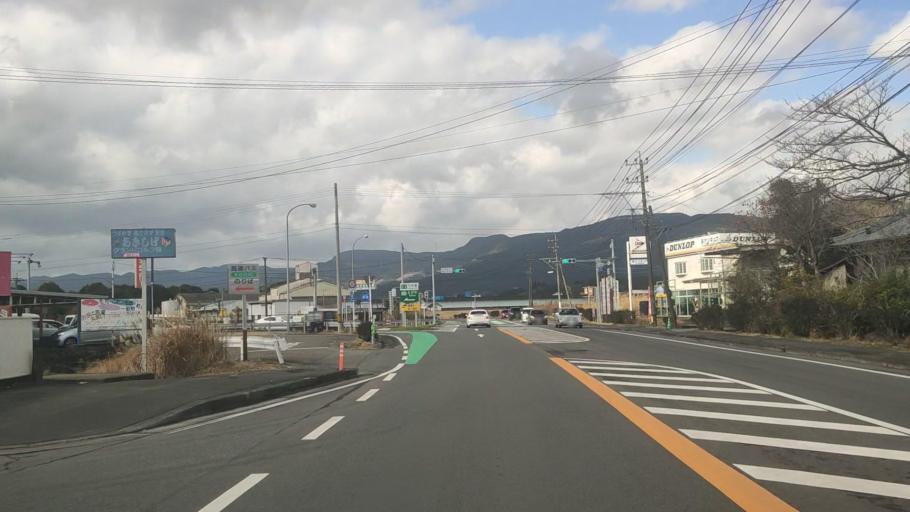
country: JP
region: Kumamoto
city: Hitoyoshi
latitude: 32.0516
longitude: 130.8050
